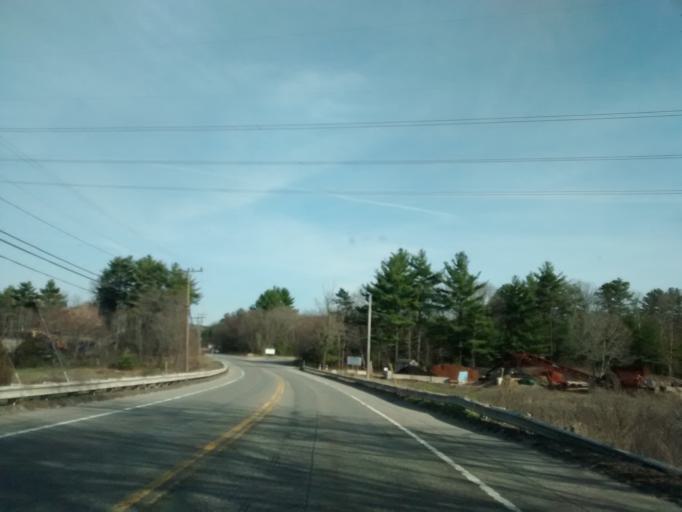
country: US
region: Massachusetts
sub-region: Worcester County
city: Millville
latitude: 42.0338
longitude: -71.6174
